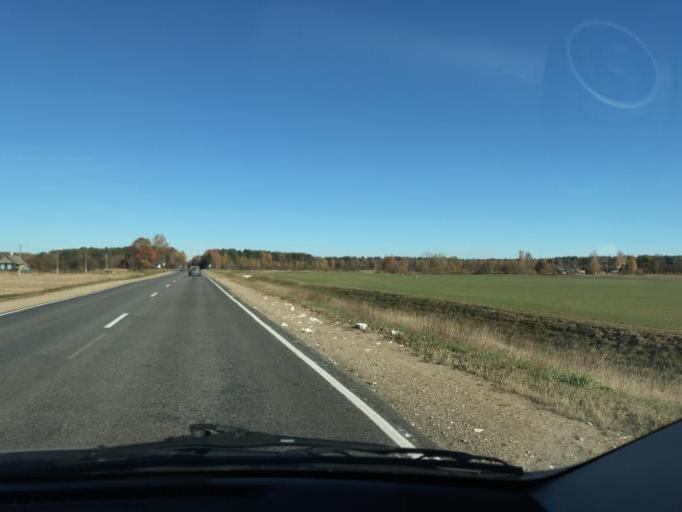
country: BY
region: Vitebsk
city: Lyepyel'
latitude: 55.0539
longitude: 28.7514
